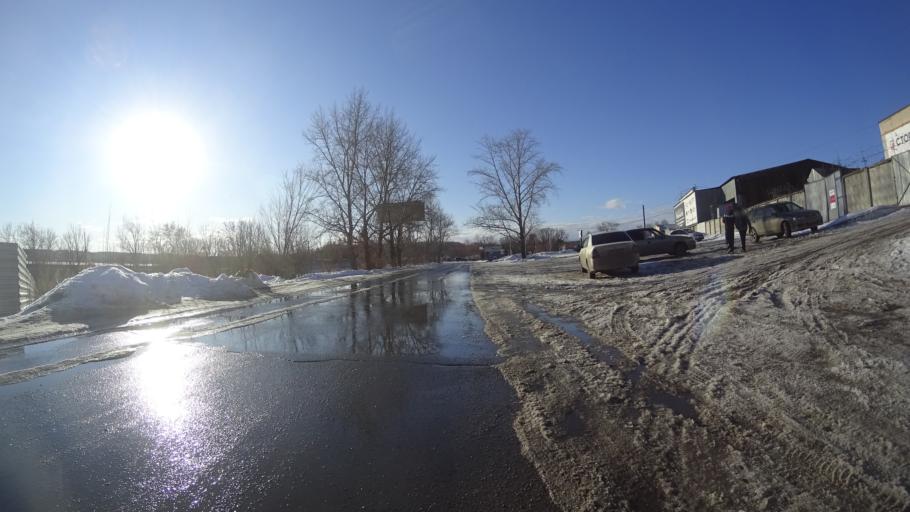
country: RU
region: Chelyabinsk
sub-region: Gorod Chelyabinsk
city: Chelyabinsk
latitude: 55.1485
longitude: 61.3057
